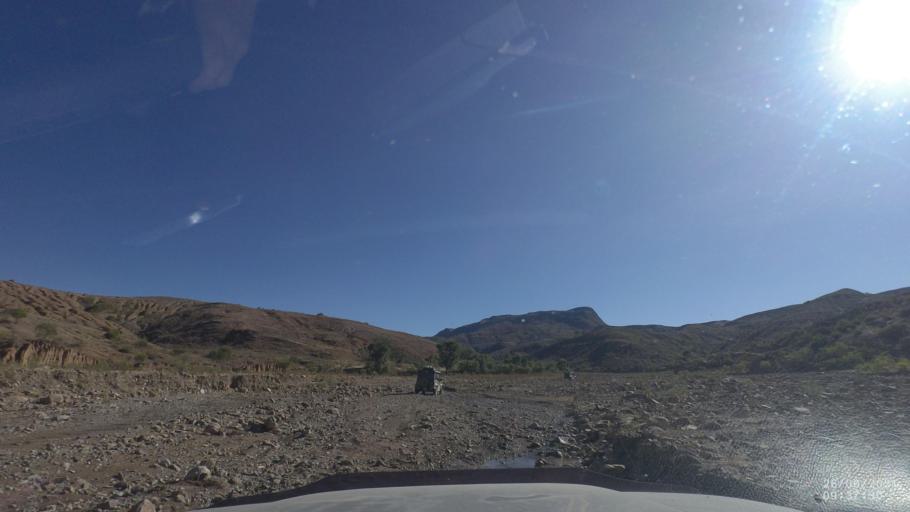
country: BO
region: Cochabamba
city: Mizque
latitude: -17.9465
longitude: -65.6350
